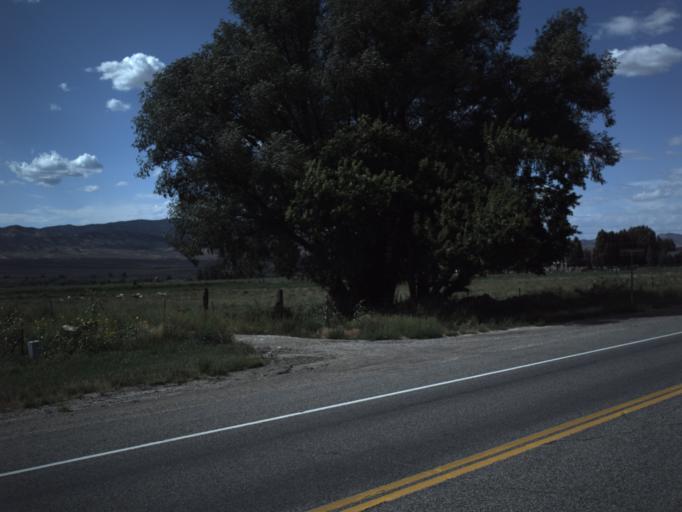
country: US
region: Utah
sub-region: Sevier County
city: Salina
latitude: 38.9668
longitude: -111.8600
